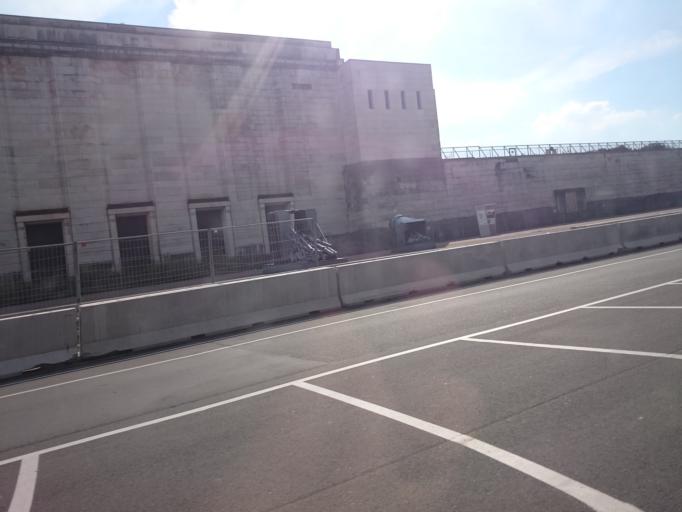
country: DE
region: Bavaria
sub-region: Regierungsbezirk Mittelfranken
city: Nuernberg
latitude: 49.4321
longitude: 11.1256
